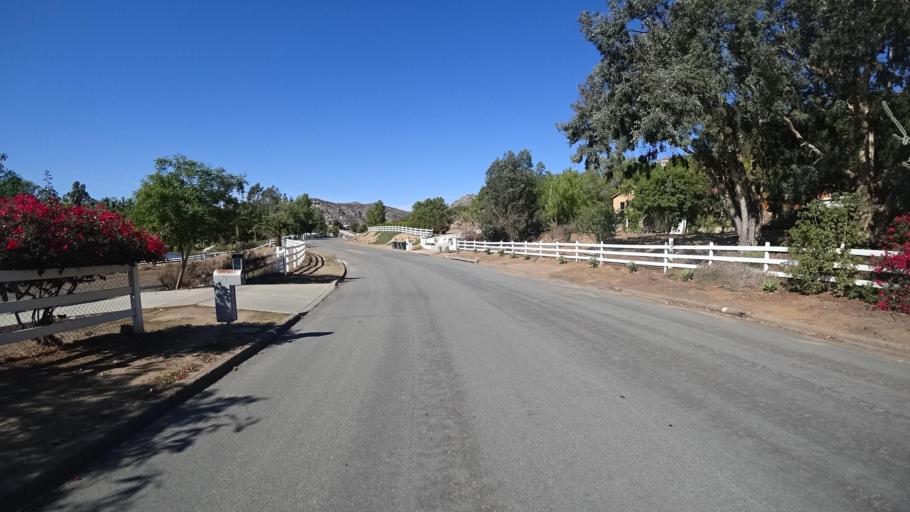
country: US
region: California
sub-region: San Diego County
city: Lakeside
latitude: 32.8670
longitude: -116.8804
